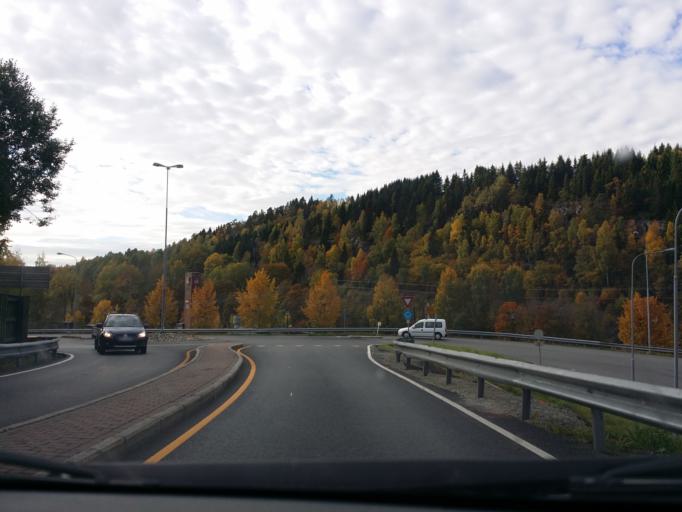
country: NO
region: Akershus
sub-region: Baerum
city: Sandvika
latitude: 59.9417
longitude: 10.5034
